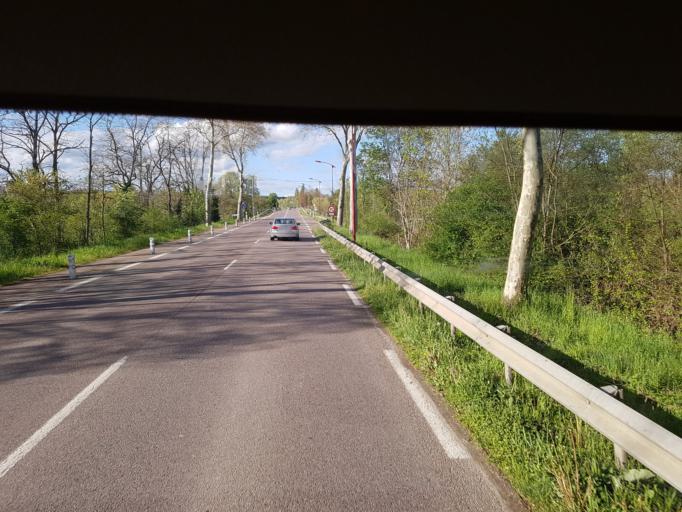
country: FR
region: Bourgogne
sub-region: Departement de l'Yonne
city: Saint-Florentin
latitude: 47.9913
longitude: 3.7342
